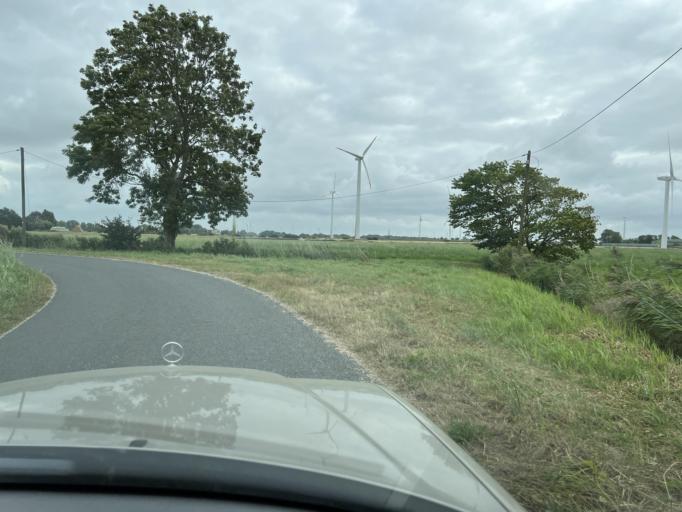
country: DE
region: Schleswig-Holstein
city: Groven
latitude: 54.2999
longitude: 9.0005
